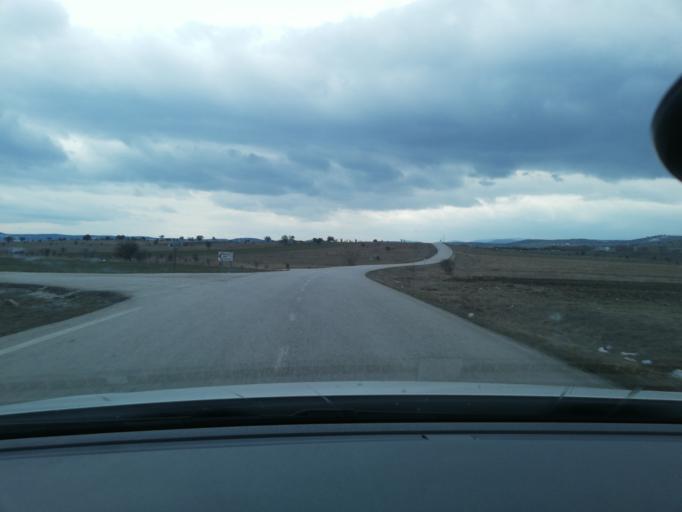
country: TR
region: Bolu
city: Gerede
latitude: 40.7141
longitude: 32.2257
